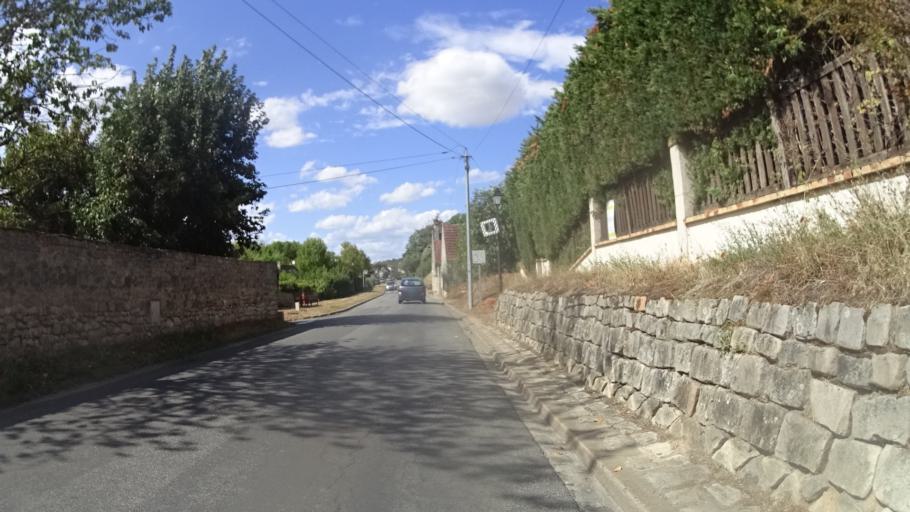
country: FR
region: Ile-de-France
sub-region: Departement de l'Essonne
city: Boutigny-sur-Essonne
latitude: 48.4304
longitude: 2.3818
